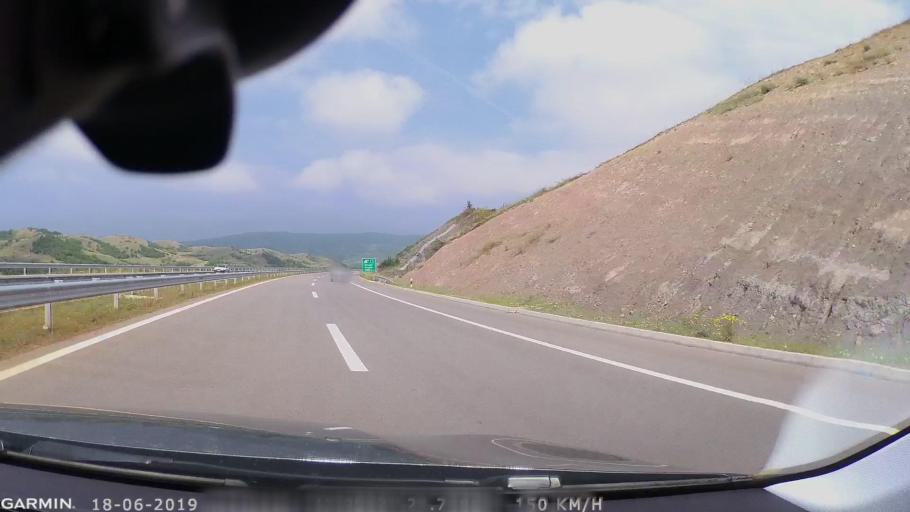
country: MK
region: Sveti Nikole
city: Gorobinci
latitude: 41.9280
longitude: 21.8312
